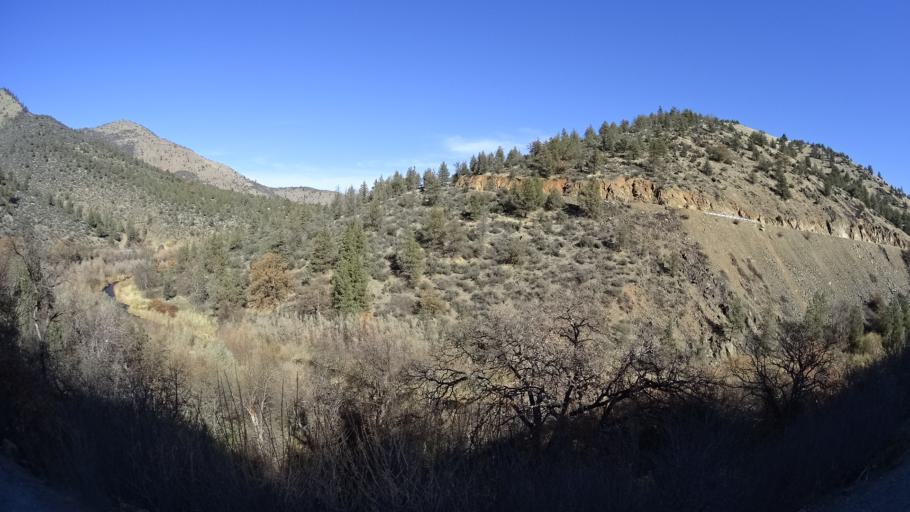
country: US
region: California
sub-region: Siskiyou County
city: Yreka
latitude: 41.7910
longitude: -122.6098
